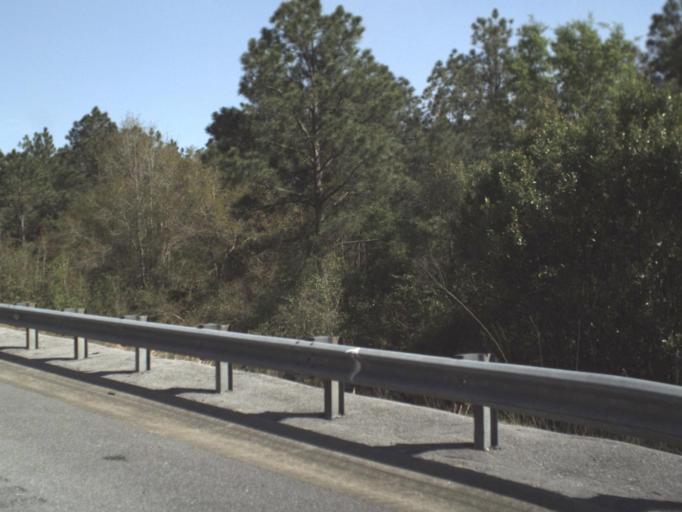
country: US
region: Florida
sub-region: Okaloosa County
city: Crestview
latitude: 30.7145
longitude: -86.6351
